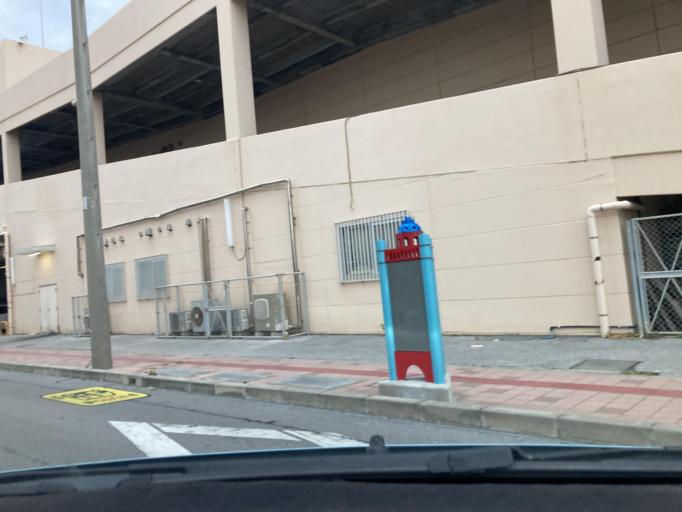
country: JP
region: Okinawa
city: Chatan
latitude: 26.3138
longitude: 127.7568
